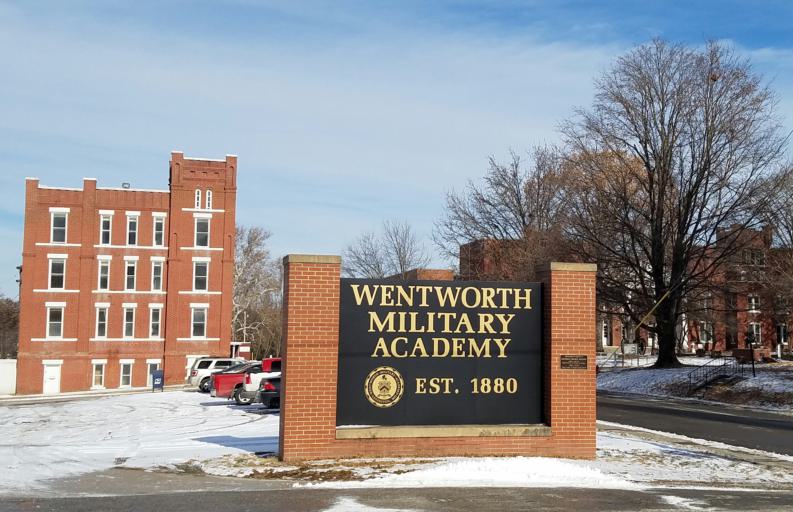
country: US
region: Missouri
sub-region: Lafayette County
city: Lexington
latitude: 39.1858
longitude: -93.8741
